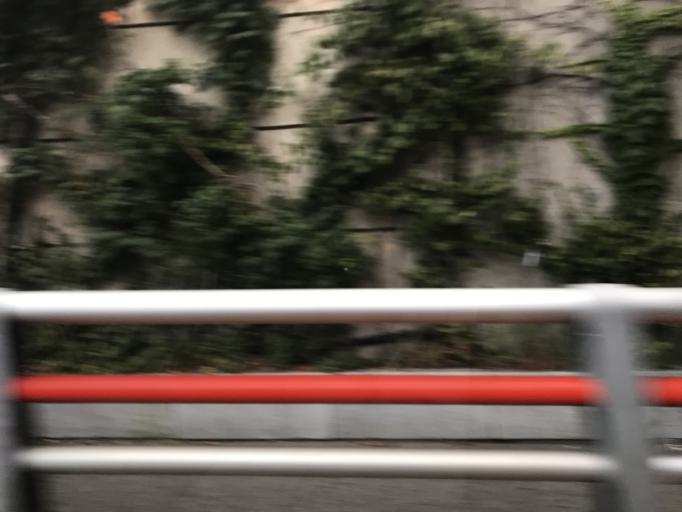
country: KR
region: Seoul
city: Seoul
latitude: 37.5683
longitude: 126.9479
